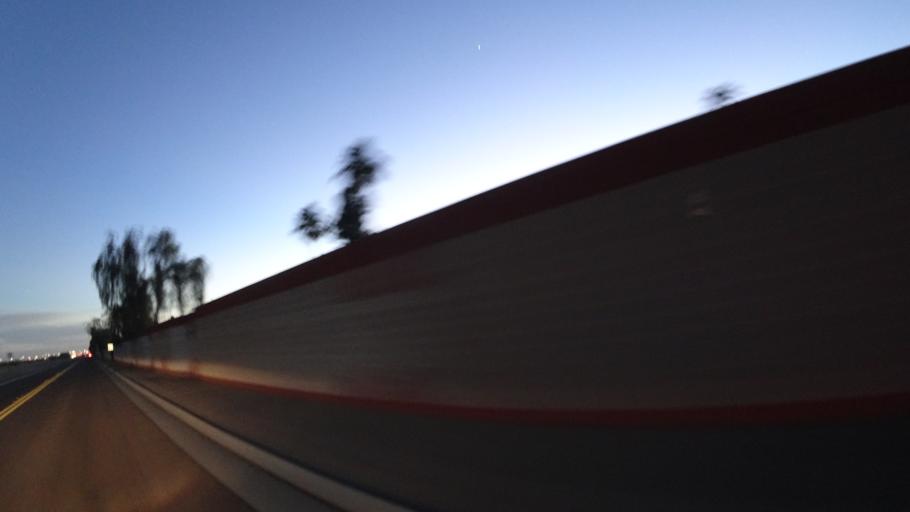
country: US
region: Arizona
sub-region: Maricopa County
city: Scottsdale
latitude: 33.4741
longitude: -111.8919
